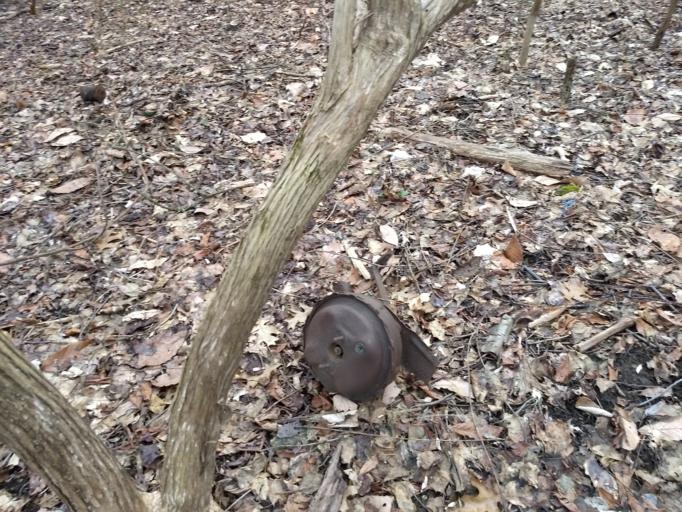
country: US
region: Pennsylvania
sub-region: Allegheny County
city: Homestead
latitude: 40.4105
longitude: -79.9321
